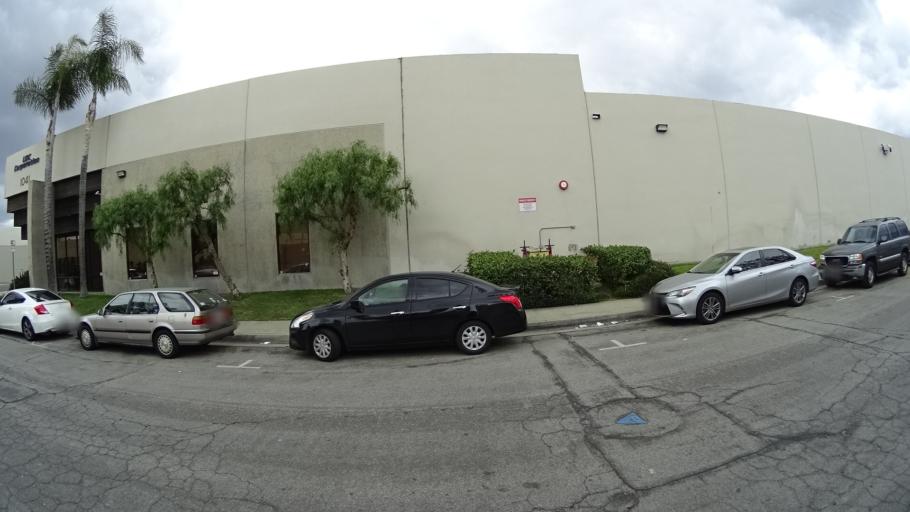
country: US
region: California
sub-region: Orange County
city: Placentia
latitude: 33.8488
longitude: -117.8580
